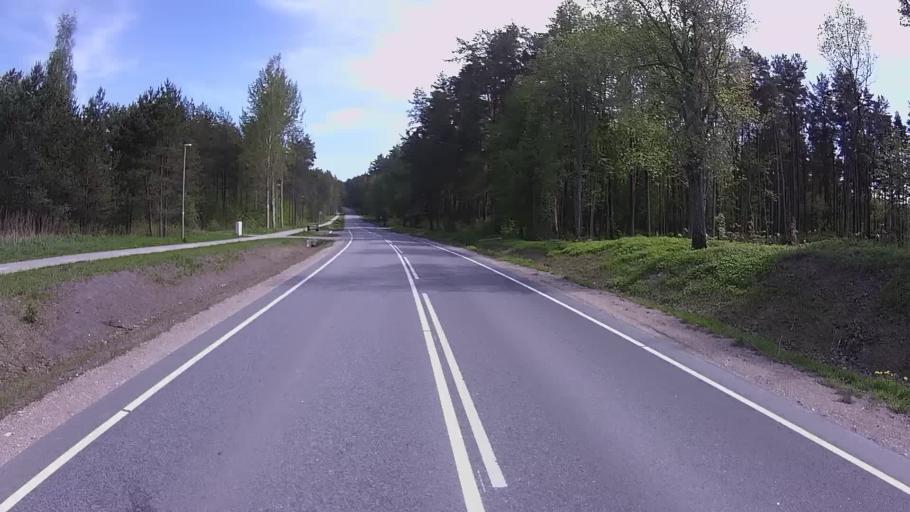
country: EE
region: Valgamaa
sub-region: Valga linn
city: Valga
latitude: 57.7638
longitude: 26.0879
